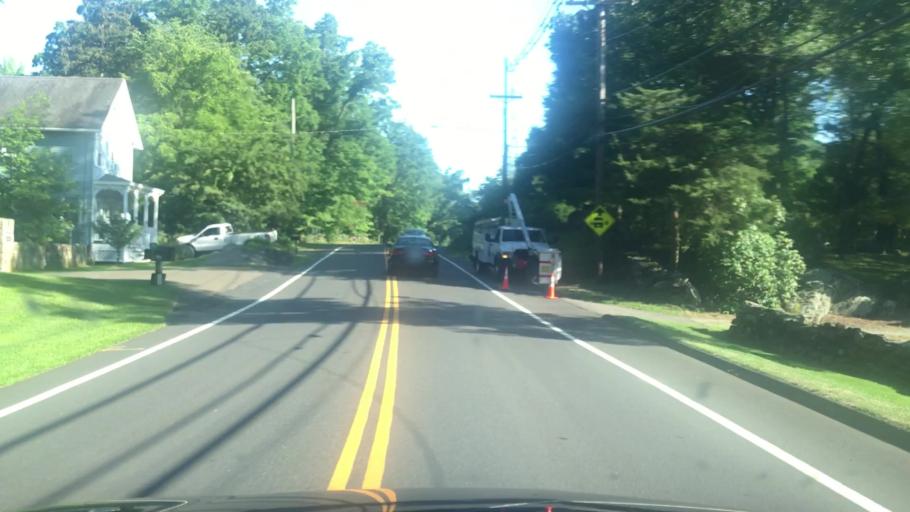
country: US
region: Connecticut
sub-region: Fairfield County
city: Pemberwick
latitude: 41.0248
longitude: -73.6513
